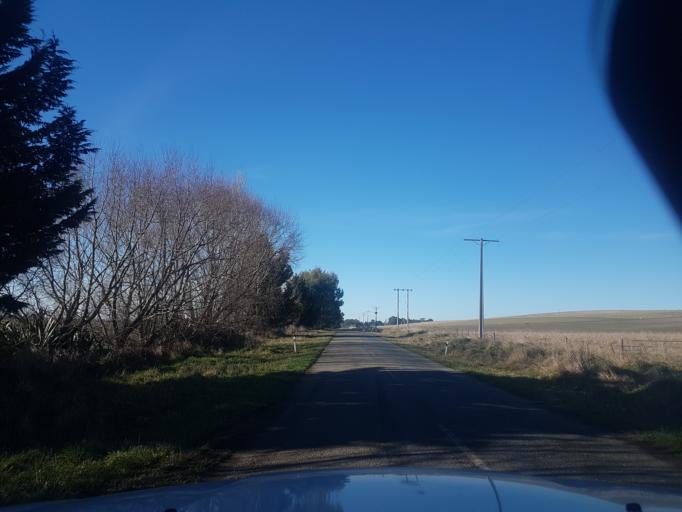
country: NZ
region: Canterbury
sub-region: Timaru District
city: Pleasant Point
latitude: -44.2903
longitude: 171.0668
